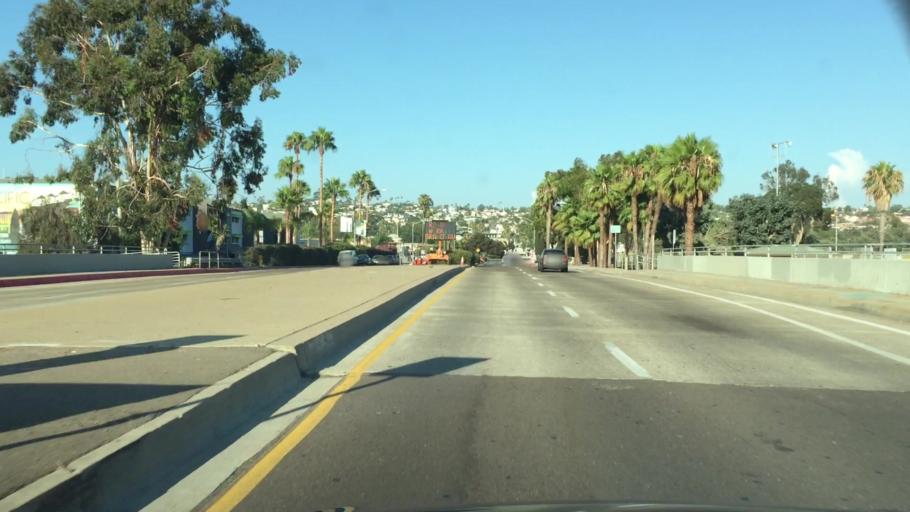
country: US
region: California
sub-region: San Diego County
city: La Jolla
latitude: 32.8018
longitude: -117.2223
